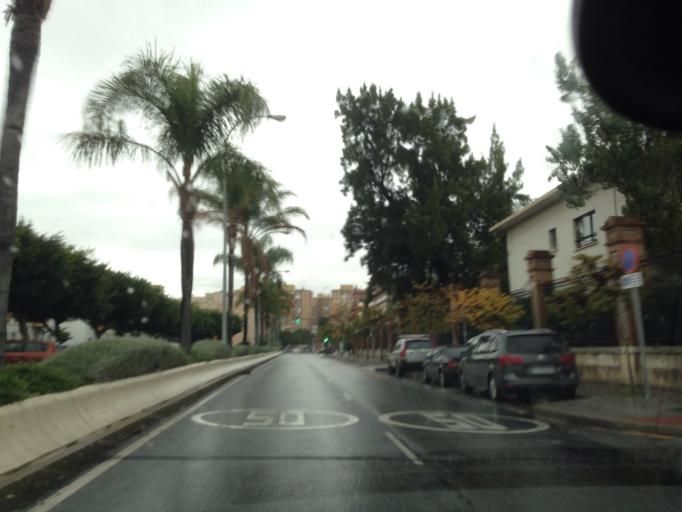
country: ES
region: Andalusia
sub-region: Provincia de Malaga
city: Malaga
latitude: 36.6985
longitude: -4.4406
